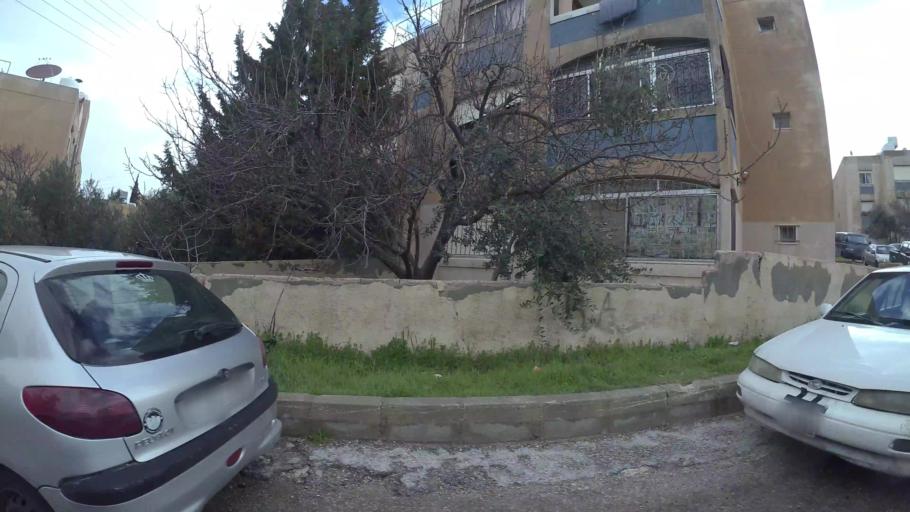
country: JO
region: Amman
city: Al Jubayhah
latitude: 32.0588
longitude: 35.8850
